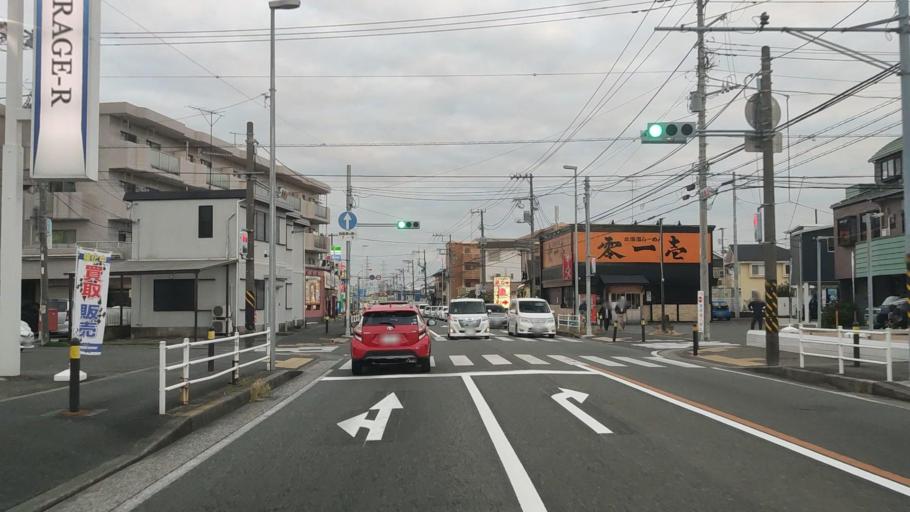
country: JP
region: Kanagawa
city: Minami-rinkan
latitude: 35.4198
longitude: 139.4691
